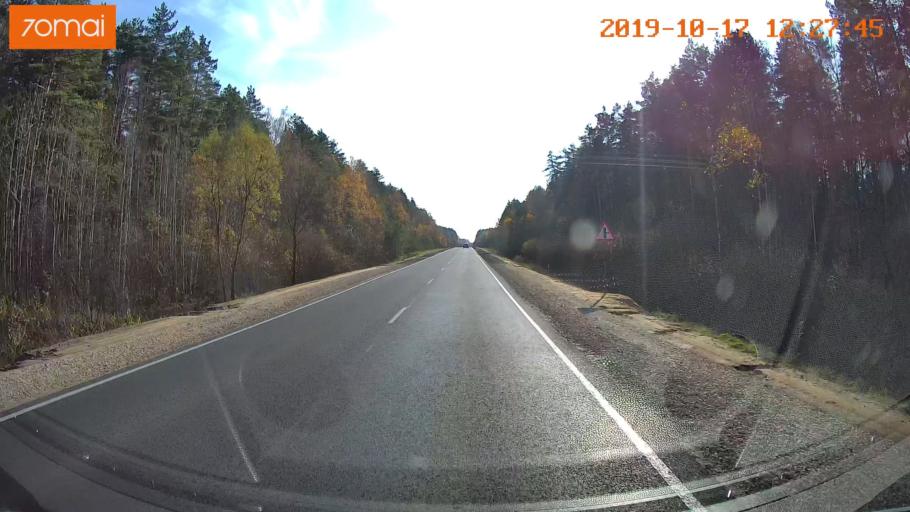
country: RU
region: Rjazan
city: Syntul
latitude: 54.9991
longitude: 41.2649
